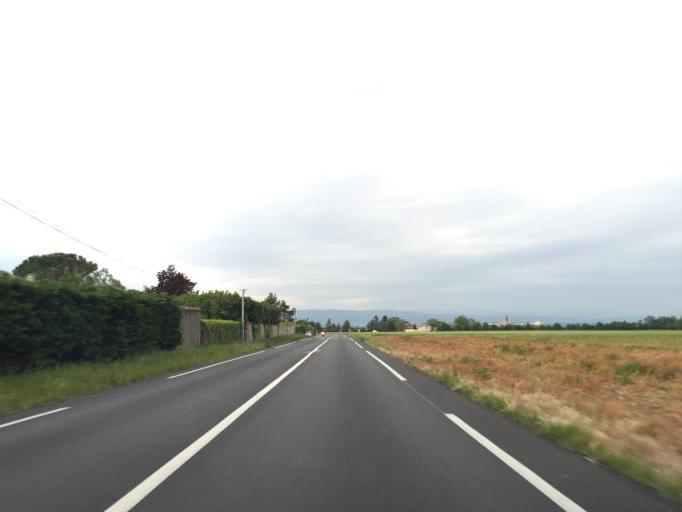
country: FR
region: Rhone-Alpes
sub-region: Departement de la Drome
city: Chabeuil
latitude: 44.9115
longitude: 5.0319
